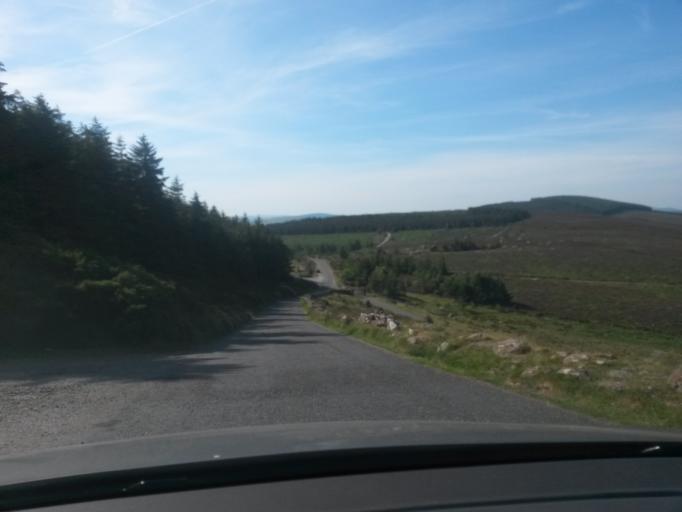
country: IE
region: Leinster
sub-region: Wicklow
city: Enniskerry
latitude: 53.0978
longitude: -6.2514
